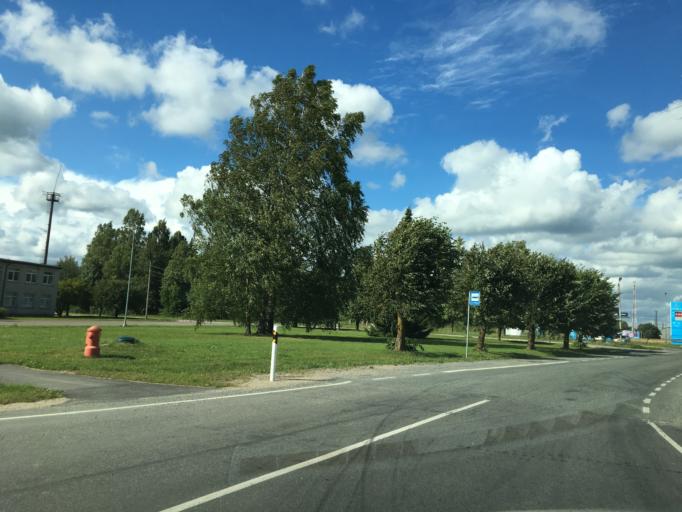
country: EE
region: Paernumaa
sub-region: Vaendra vald (alev)
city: Vandra
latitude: 58.6516
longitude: 25.0224
